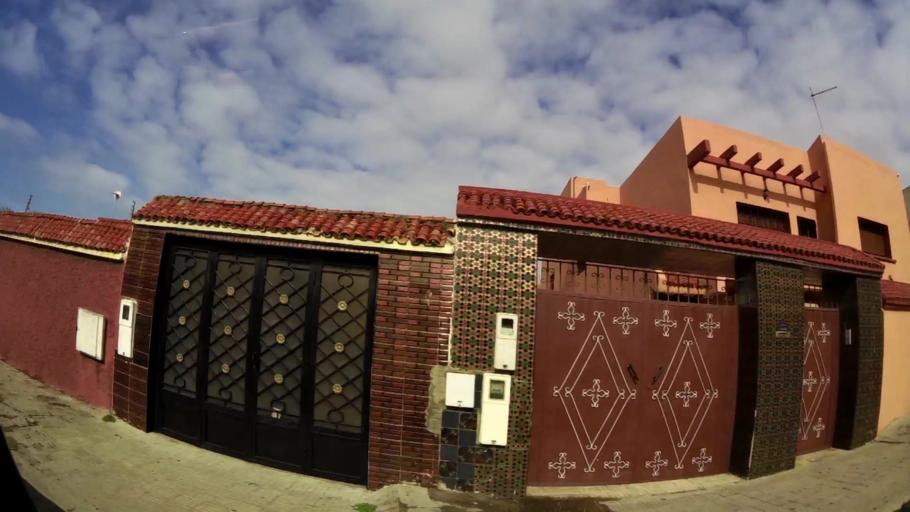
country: MA
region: Grand Casablanca
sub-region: Mohammedia
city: Mohammedia
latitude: 33.6950
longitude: -7.3869
